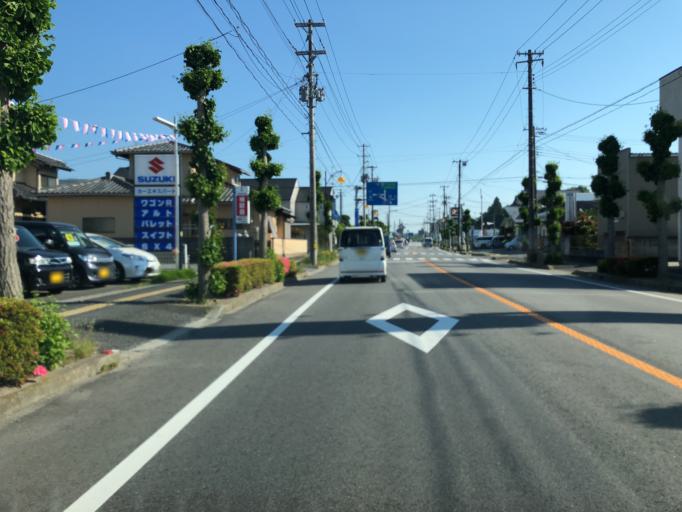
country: JP
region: Ibaraki
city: Kitaibaraki
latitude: 36.9133
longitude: 140.7746
